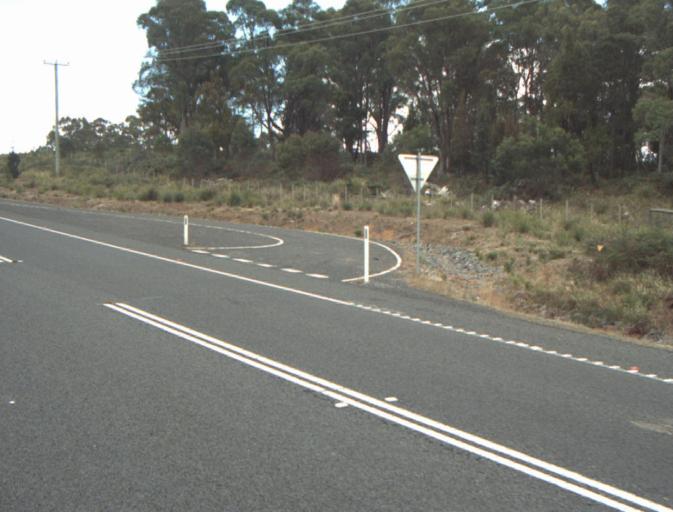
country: AU
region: Tasmania
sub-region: Launceston
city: Mayfield
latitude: -41.2735
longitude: 147.0360
